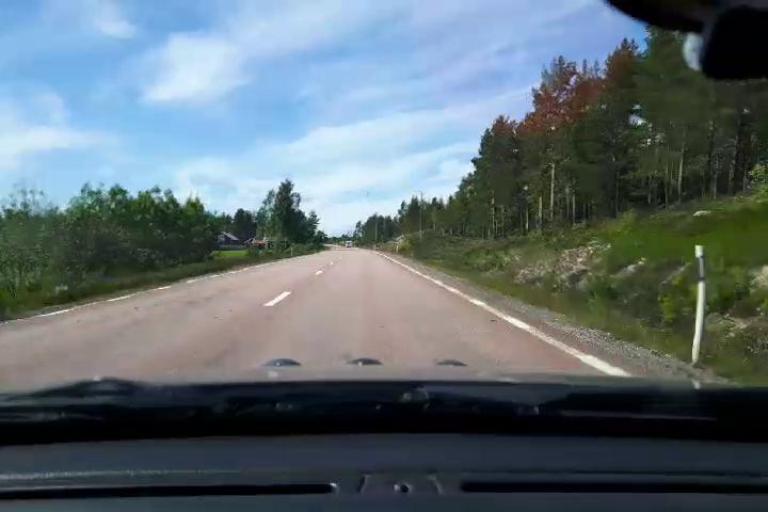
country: SE
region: Gaevleborg
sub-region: Soderhamns Kommun
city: Soderhamn
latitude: 61.1304
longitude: 16.9253
